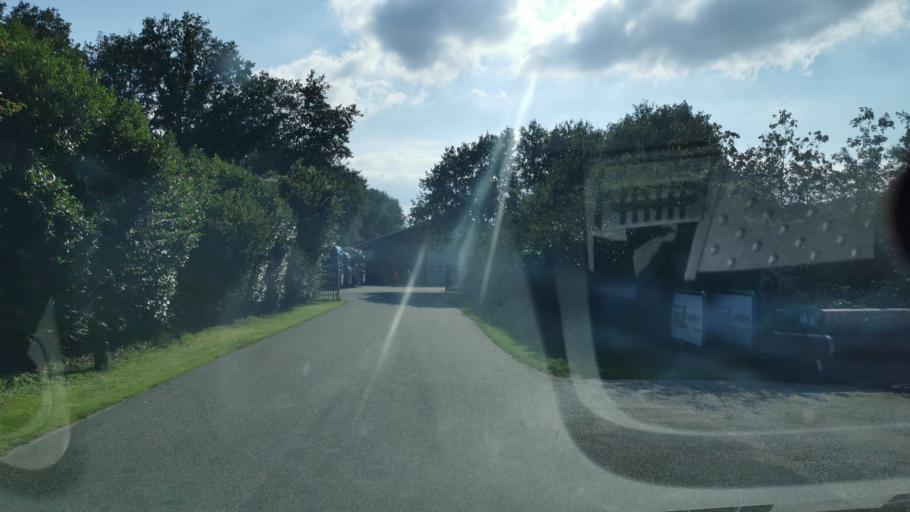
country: NL
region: Overijssel
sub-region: Gemeente Borne
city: Borne
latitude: 52.3363
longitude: 6.7949
